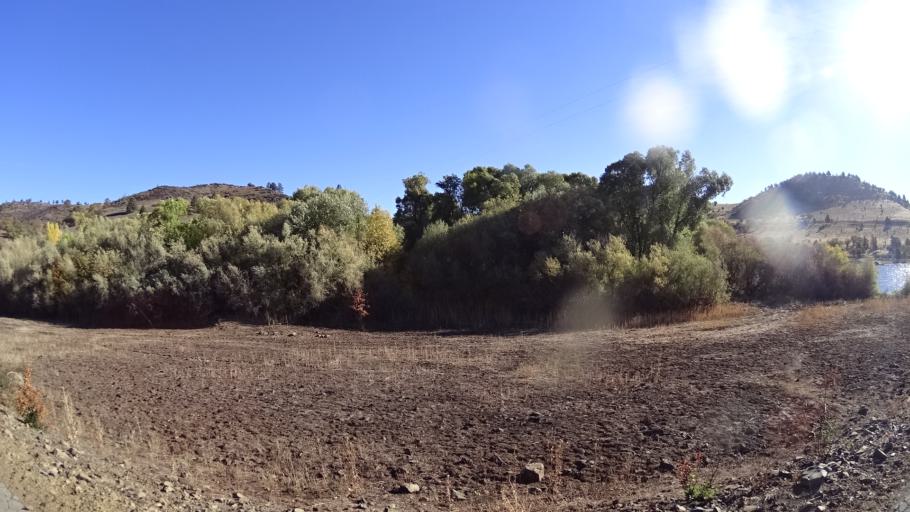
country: US
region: California
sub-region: Siskiyou County
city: Montague
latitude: 41.9738
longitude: -122.4396
